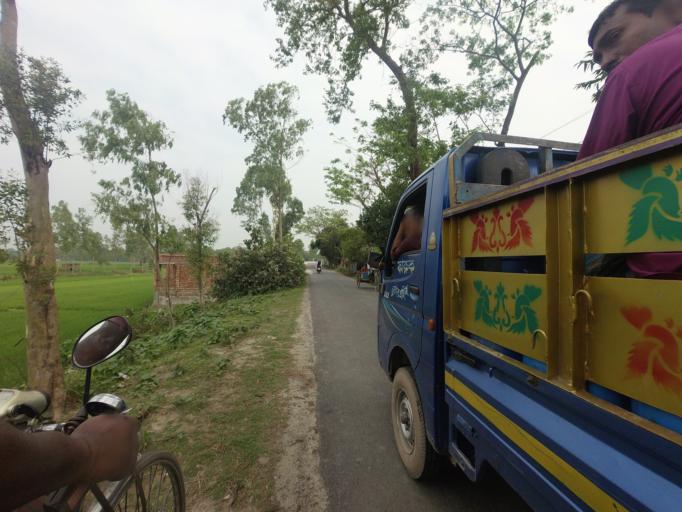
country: BD
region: Rajshahi
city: Sirajganj
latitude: 24.3641
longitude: 89.6707
